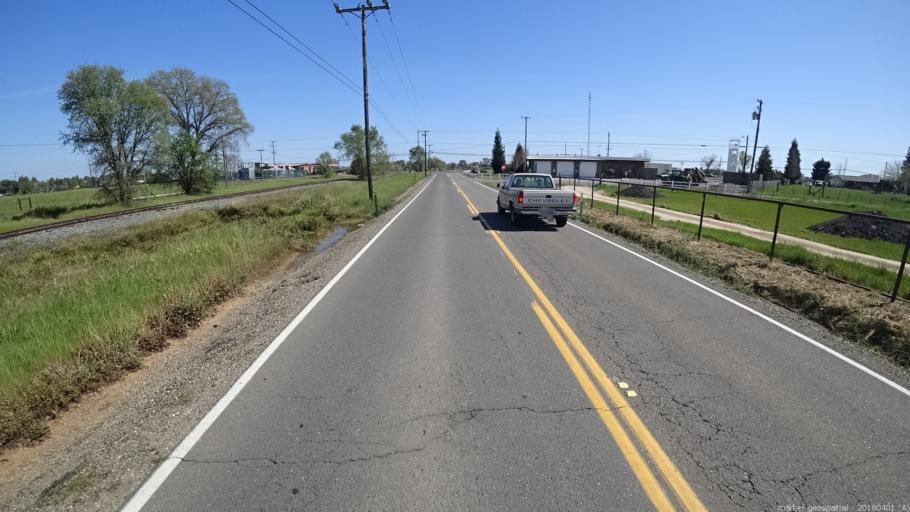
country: US
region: California
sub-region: Sacramento County
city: Wilton
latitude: 38.4021
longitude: -121.2583
